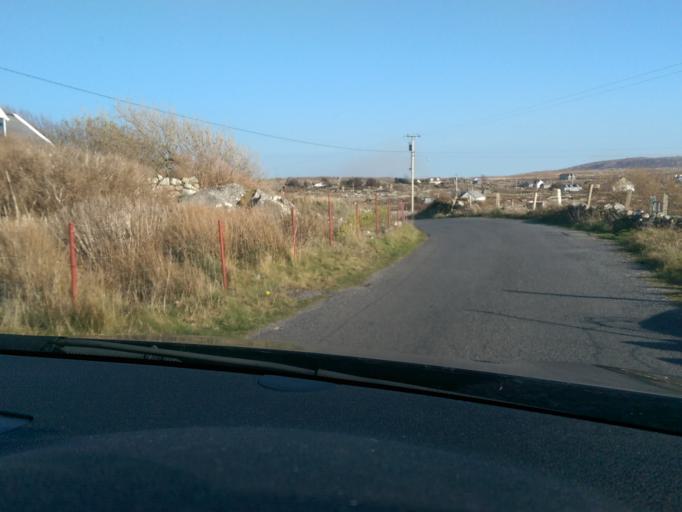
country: IE
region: Connaught
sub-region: County Galway
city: Clifden
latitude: 53.3600
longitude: -9.8781
